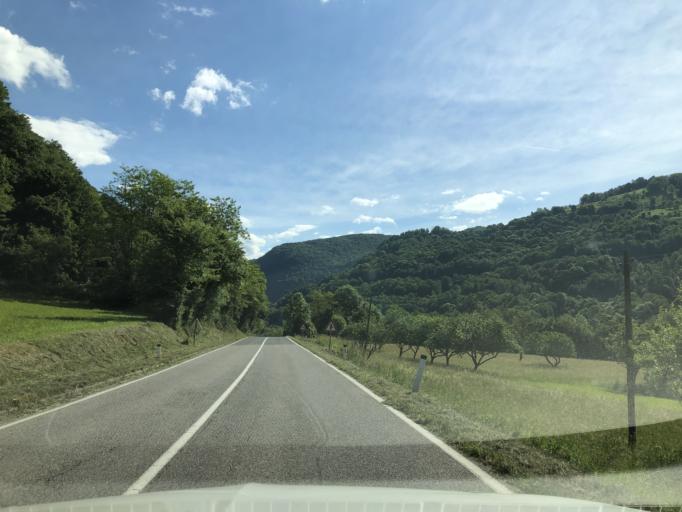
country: SI
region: Kanal
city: Kanal
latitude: 46.1079
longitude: 13.6793
